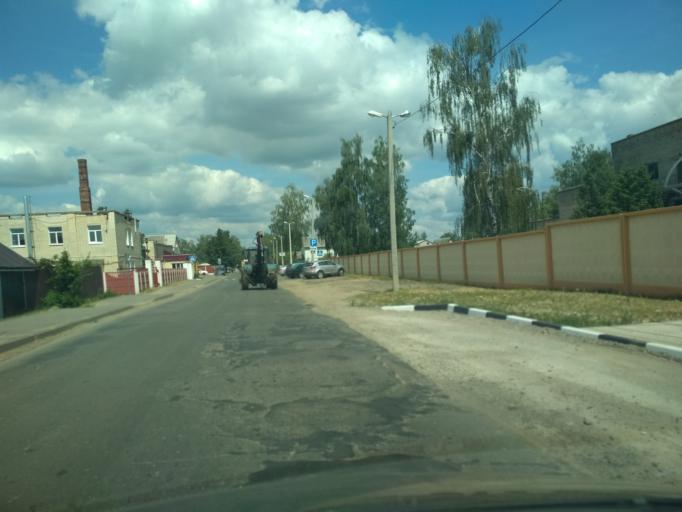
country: BY
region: Minsk
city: Mar''ina Horka
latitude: 53.5132
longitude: 28.1548
